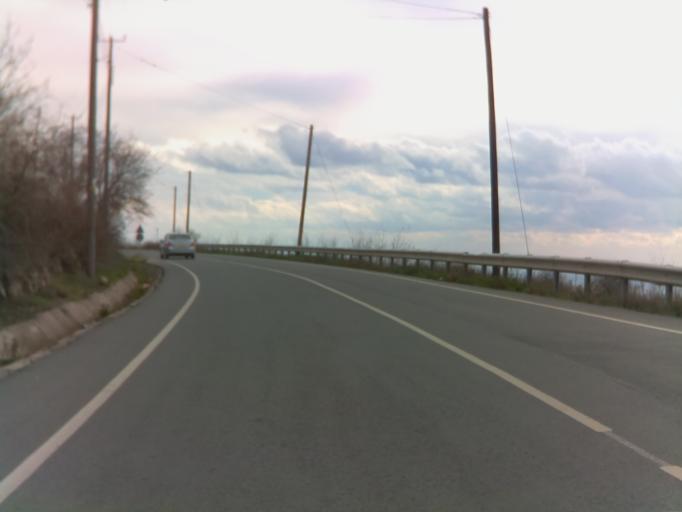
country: CY
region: Pafos
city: Pegeia
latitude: 34.9183
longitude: 32.4204
